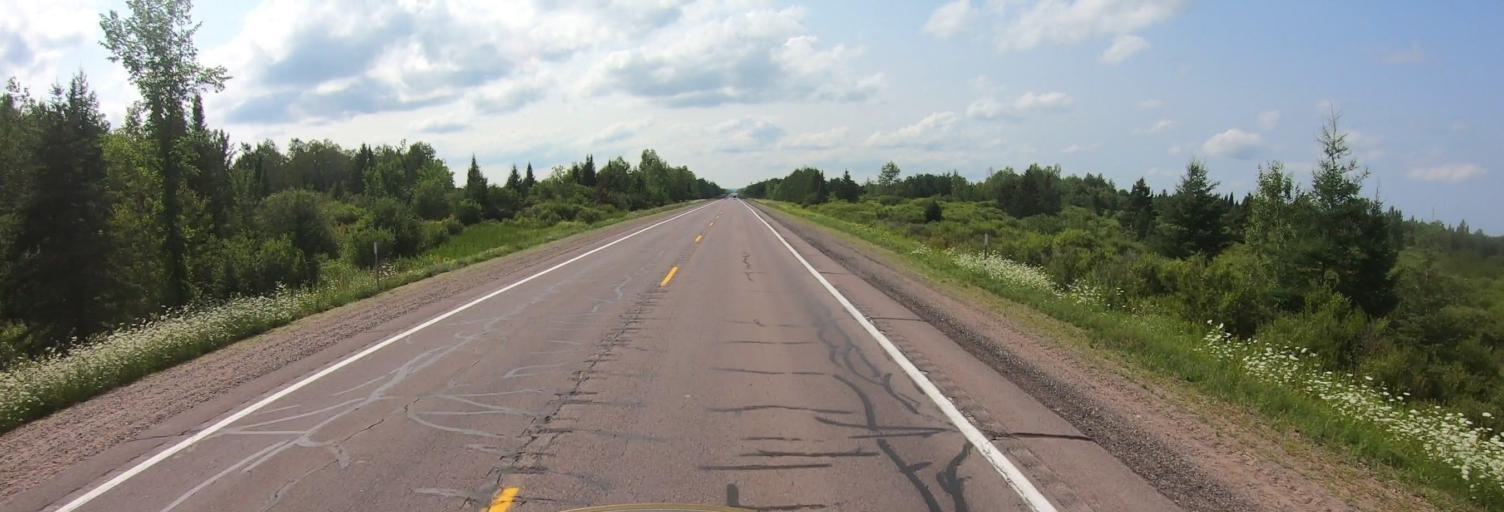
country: US
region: Michigan
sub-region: Ontonagon County
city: Ontonagon
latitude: 46.5544
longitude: -89.3893
